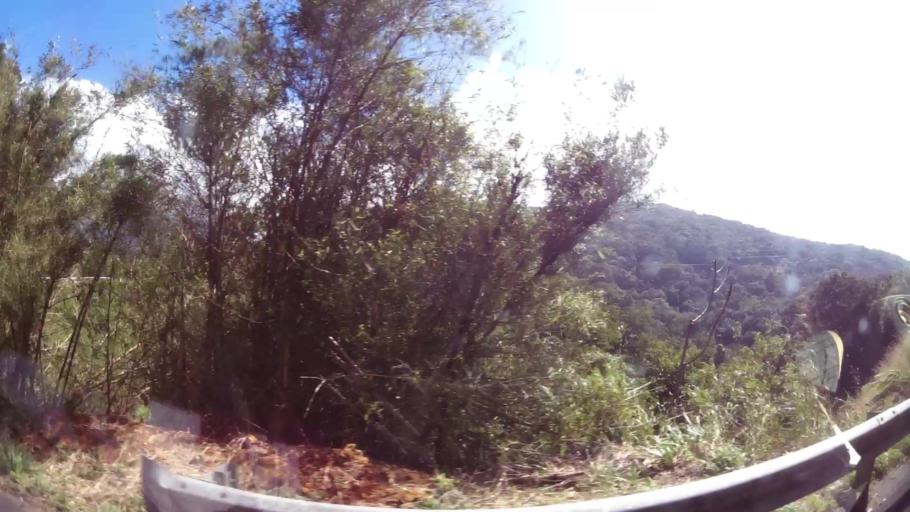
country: DM
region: Saint Paul
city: Pont Casse
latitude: 15.3545
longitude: -61.3585
